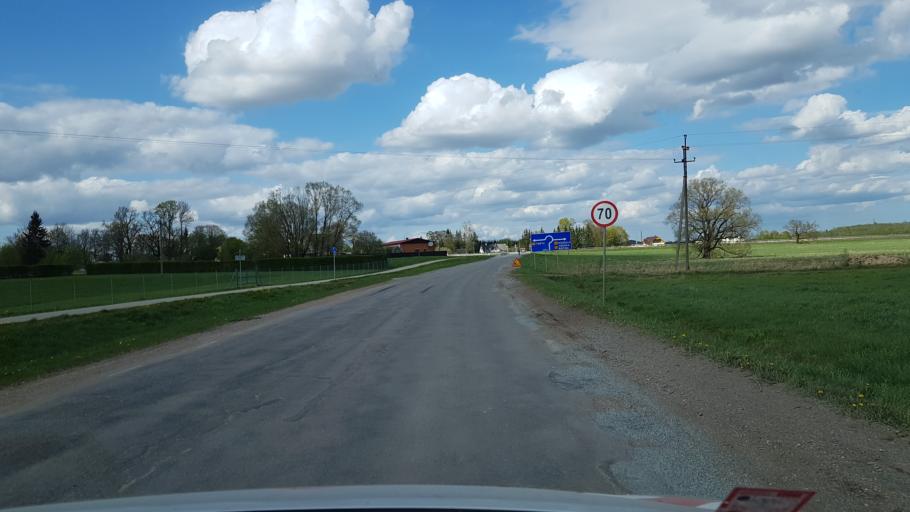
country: EE
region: Tartu
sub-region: Tartu linn
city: Tartu
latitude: 58.3692
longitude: 26.7984
